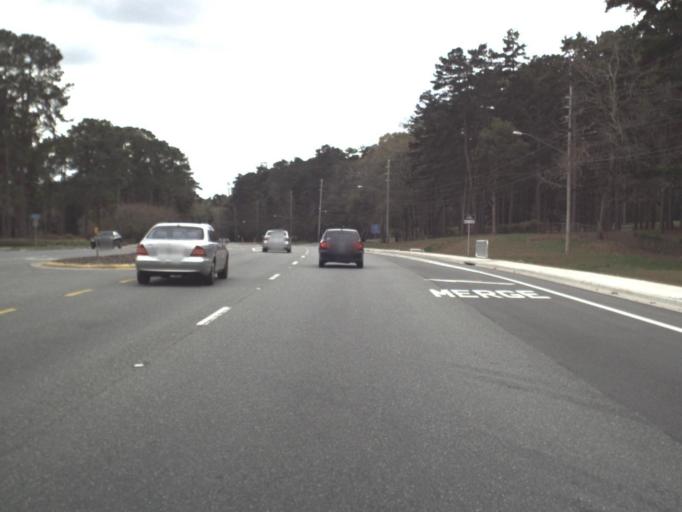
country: US
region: Florida
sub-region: Leon County
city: Tallahassee
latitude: 30.4970
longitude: -84.2541
